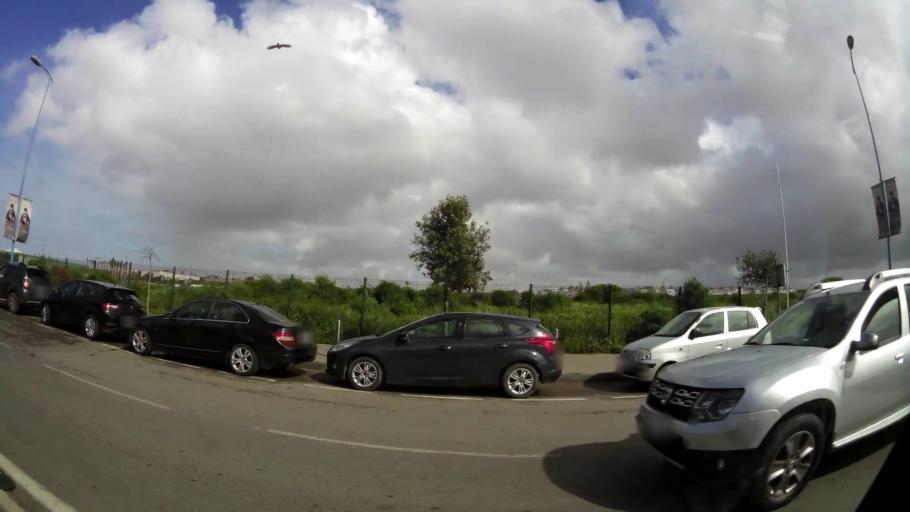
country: MA
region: Grand Casablanca
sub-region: Casablanca
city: Casablanca
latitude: 33.5764
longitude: -7.7050
